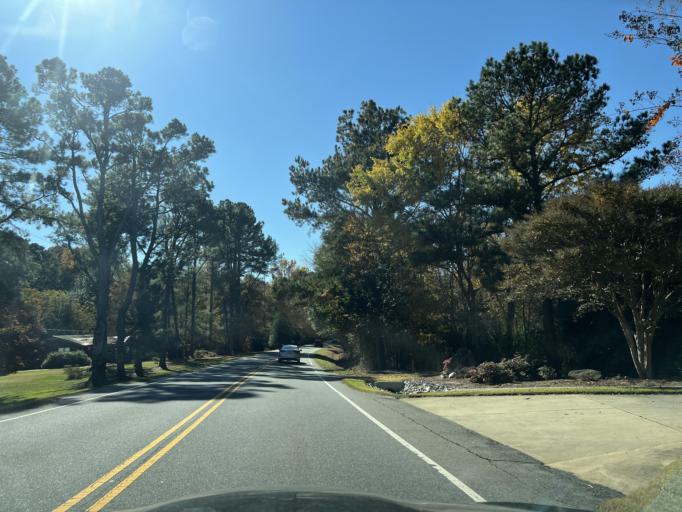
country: US
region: North Carolina
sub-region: Wake County
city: Fuquay-Varina
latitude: 35.6382
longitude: -78.7262
